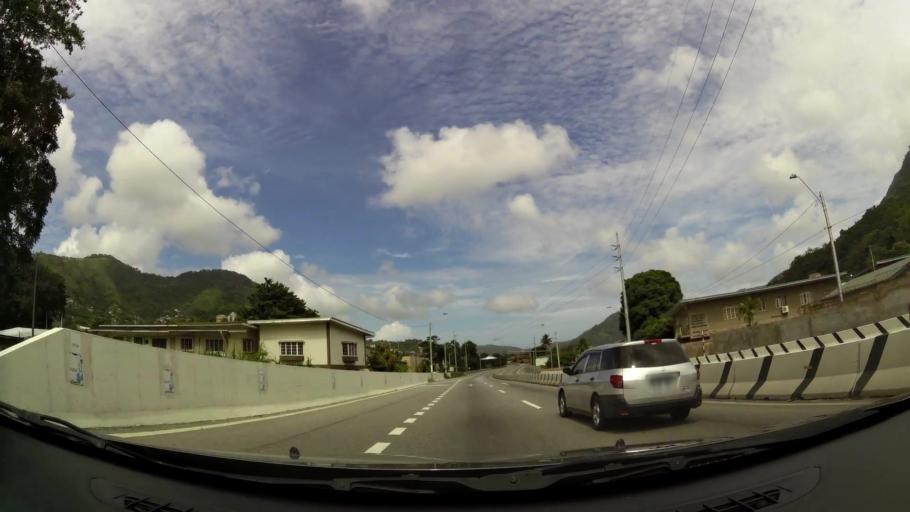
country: TT
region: Diego Martin
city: Petit Valley
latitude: 10.6886
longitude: -61.5530
